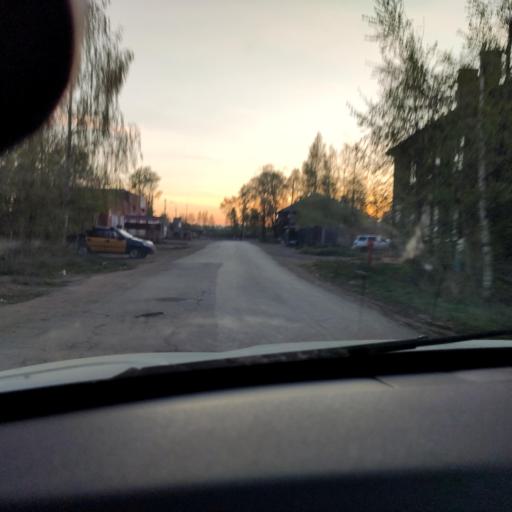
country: RU
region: Perm
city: Krasnokamsk
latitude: 58.0603
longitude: 55.8028
